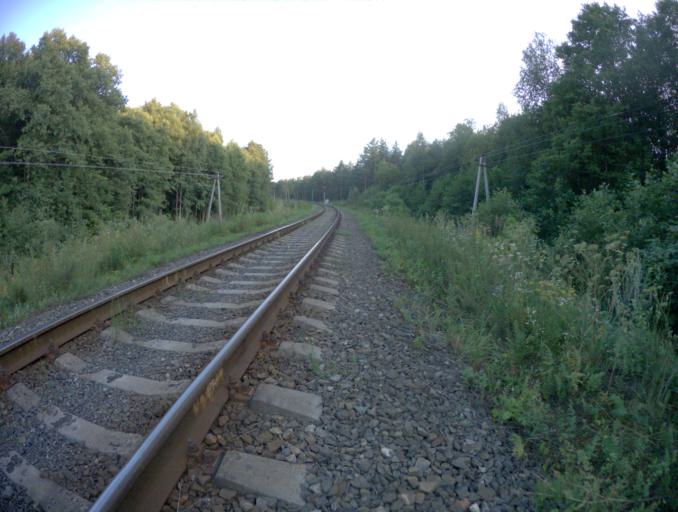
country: RU
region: Vladimir
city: Raduzhnyy
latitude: 56.0354
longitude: 40.3827
